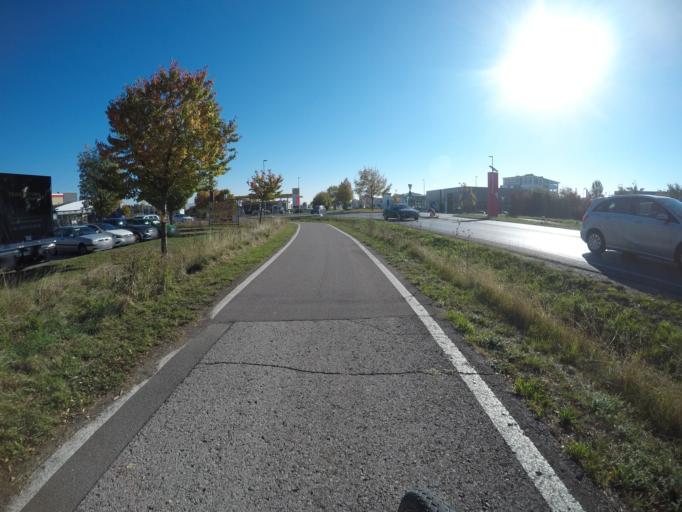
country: DE
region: Baden-Wuerttemberg
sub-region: Regierungsbezirk Stuttgart
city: Leinfelden-Echterdingen
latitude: 48.6783
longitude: 9.1918
